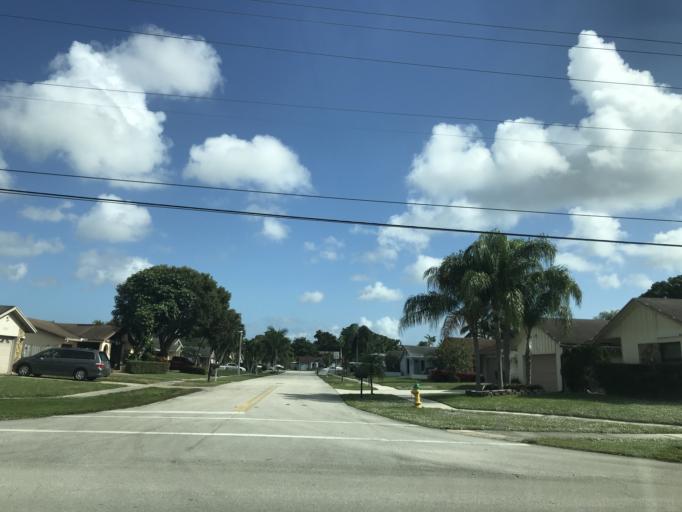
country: US
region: Florida
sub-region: Broward County
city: Coconut Creek
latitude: 26.2679
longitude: -80.1946
